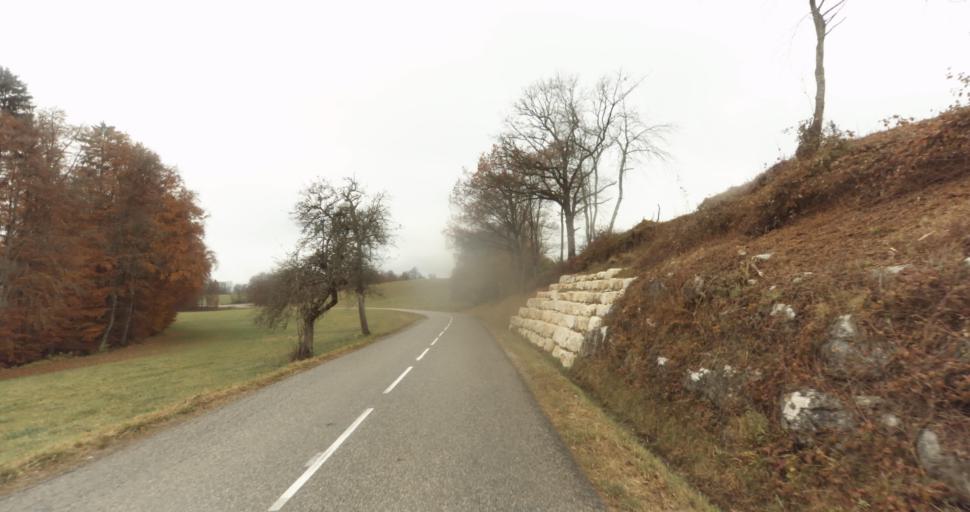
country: FR
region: Rhone-Alpes
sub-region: Departement de la Haute-Savoie
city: Evires
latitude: 46.0505
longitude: 6.1969
